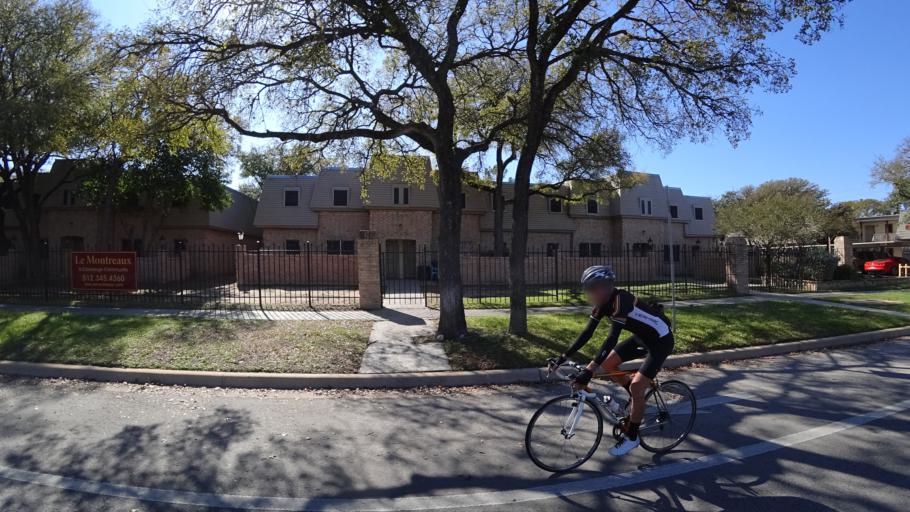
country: US
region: Texas
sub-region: Williamson County
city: Jollyville
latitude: 30.3700
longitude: -97.7463
